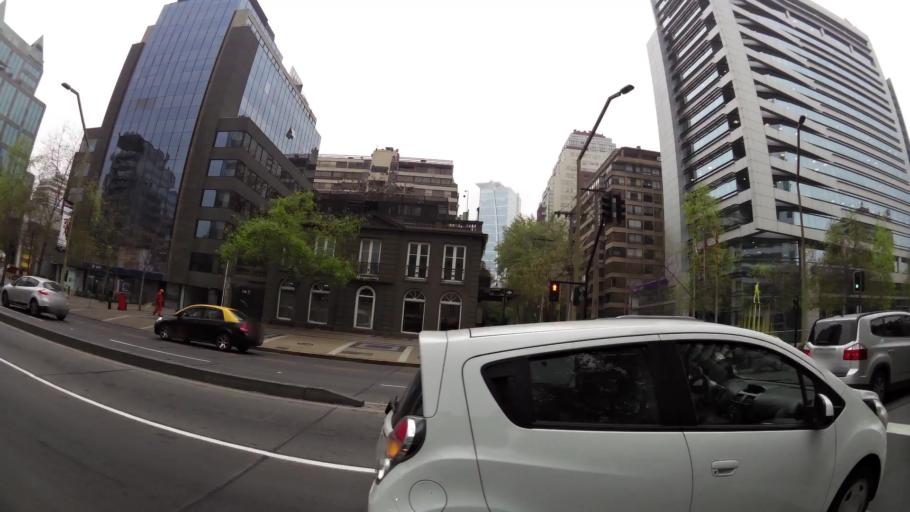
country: CL
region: Santiago Metropolitan
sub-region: Provincia de Santiago
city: Villa Presidente Frei, Nunoa, Santiago, Chile
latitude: -33.4170
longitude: -70.5974
